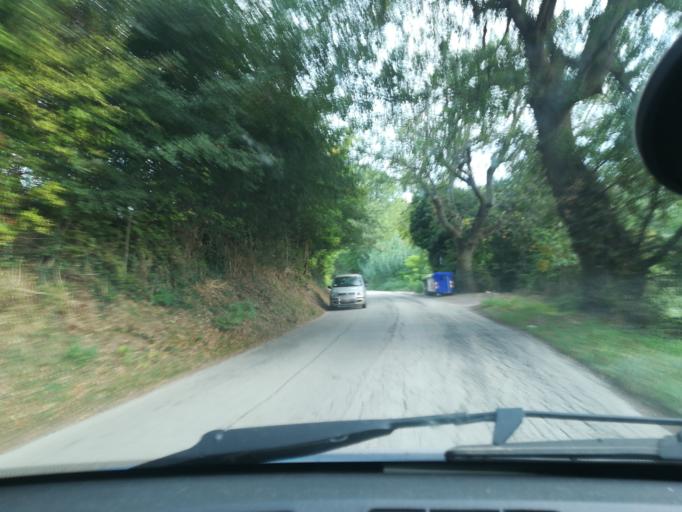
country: IT
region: The Marches
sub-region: Provincia di Macerata
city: Piediripa
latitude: 43.2982
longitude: 13.4813
